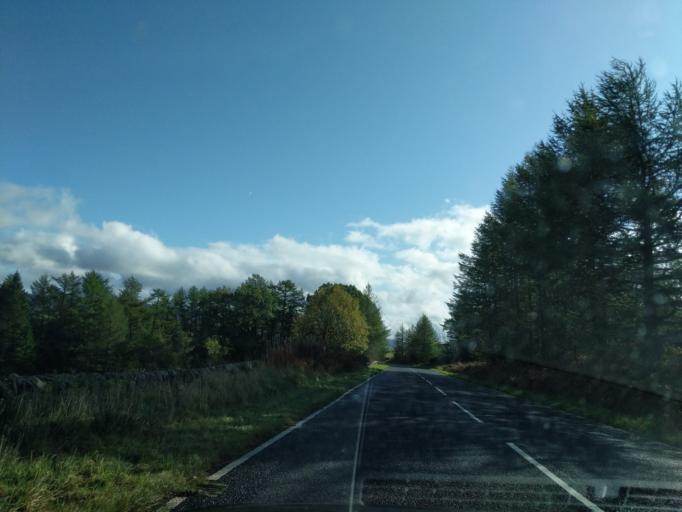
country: GB
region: Scotland
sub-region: Dumfries and Galloway
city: Moffat
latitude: 55.3570
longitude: -3.4715
